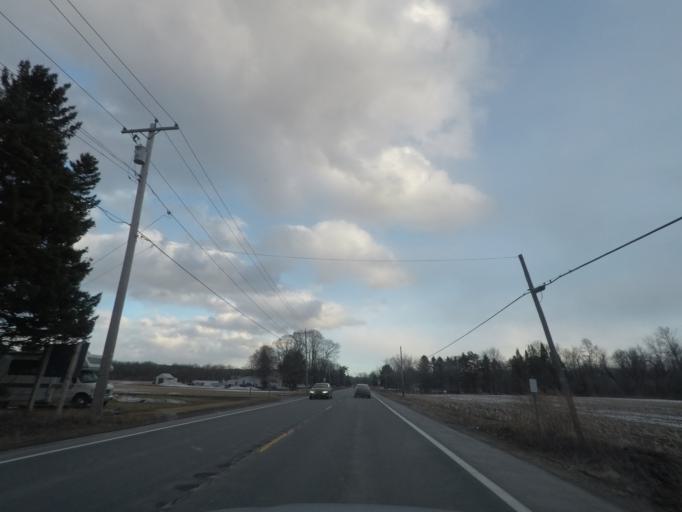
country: US
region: New York
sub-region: Herkimer County
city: Frankfort
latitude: 43.0707
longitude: -75.1041
